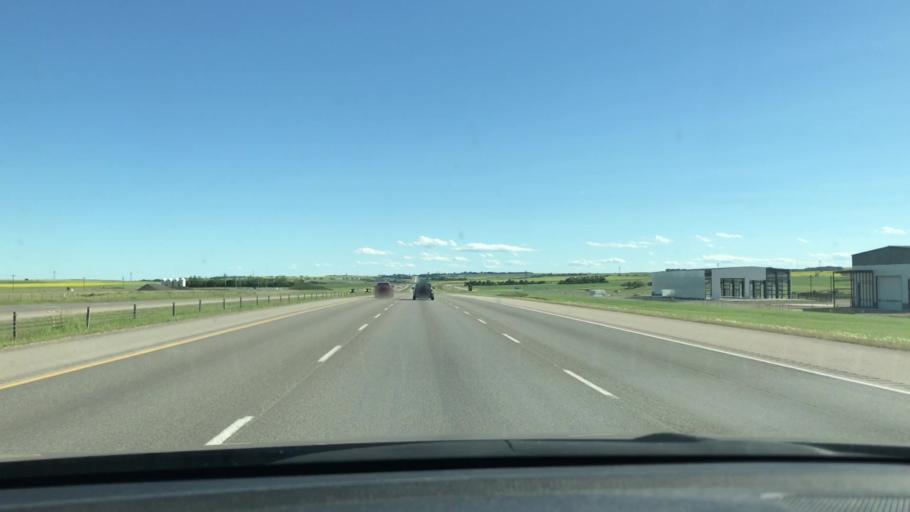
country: CA
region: Alberta
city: Crossfield
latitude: 51.4944
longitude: -114.0253
